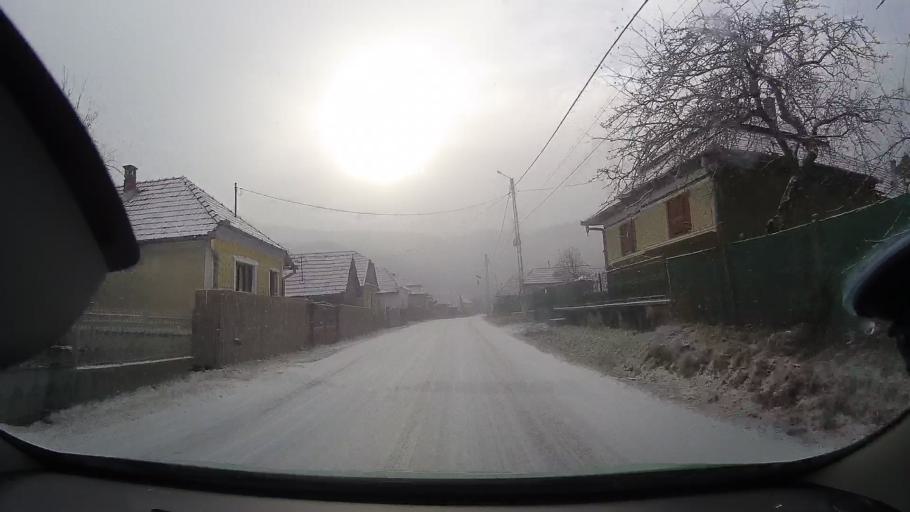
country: RO
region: Alba
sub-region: Comuna Rimetea
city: Rimetea
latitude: 46.3904
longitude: 23.5621
